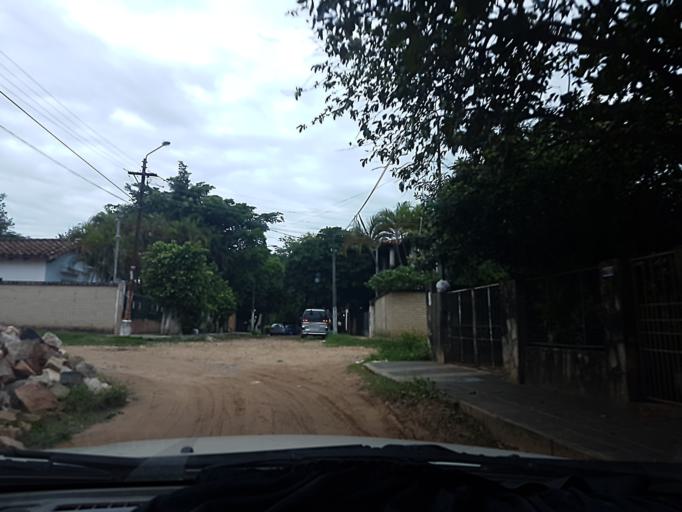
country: PY
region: Asuncion
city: Asuncion
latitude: -25.2581
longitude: -57.5744
